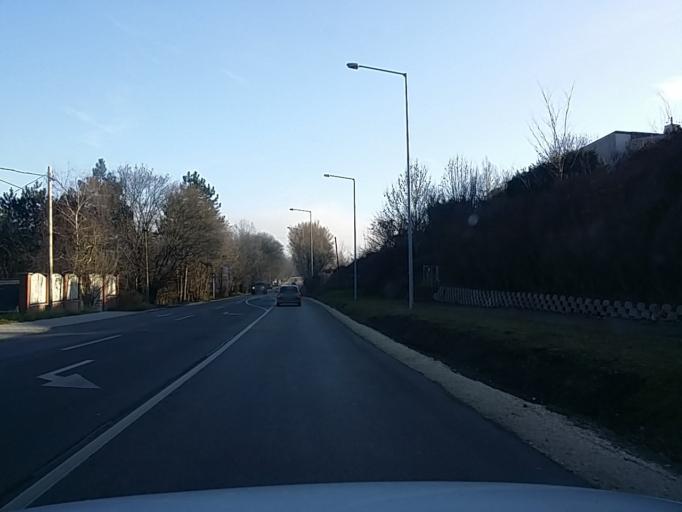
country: HU
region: Pest
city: Solymar
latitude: 47.5586
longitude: 18.9215
